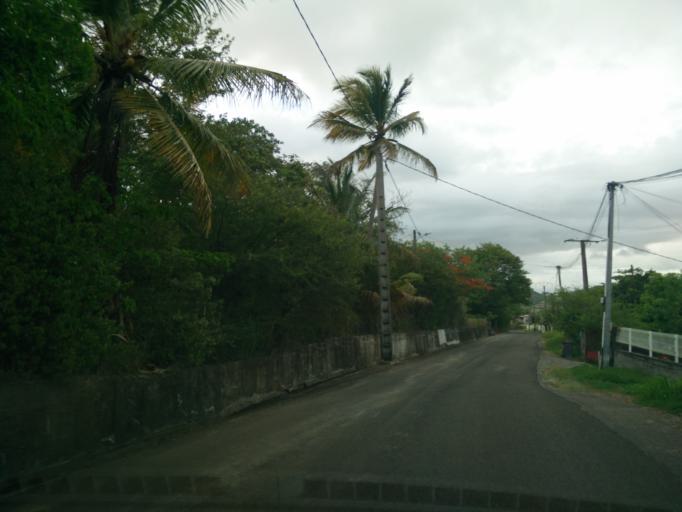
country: MQ
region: Martinique
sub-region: Martinique
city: Le Marin
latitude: 14.4499
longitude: -60.8403
